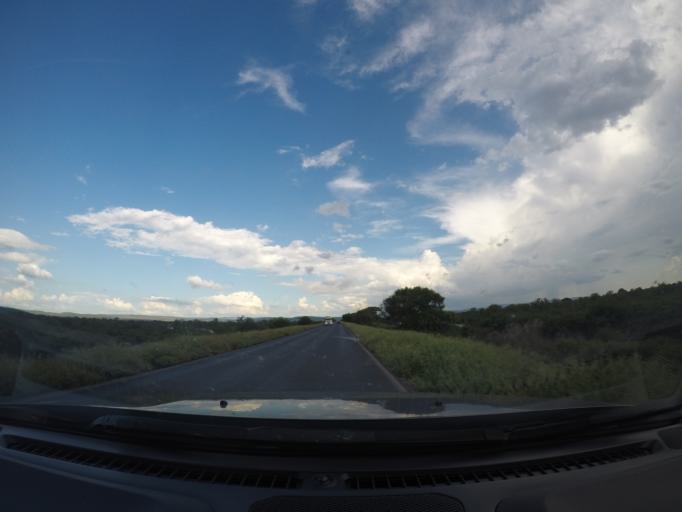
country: BR
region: Bahia
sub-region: Ibotirama
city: Ibotirama
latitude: -12.1639
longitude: -43.2826
